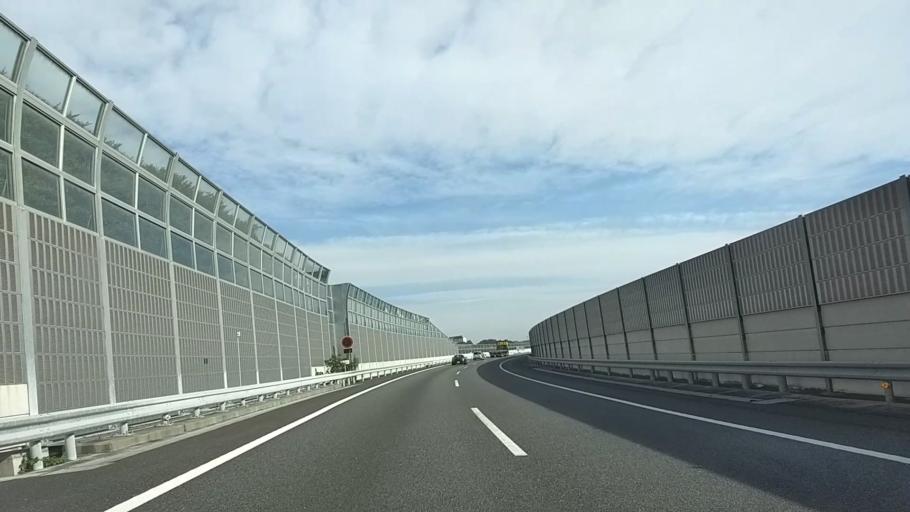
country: JP
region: Kanagawa
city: Zama
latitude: 35.4999
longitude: 139.3655
